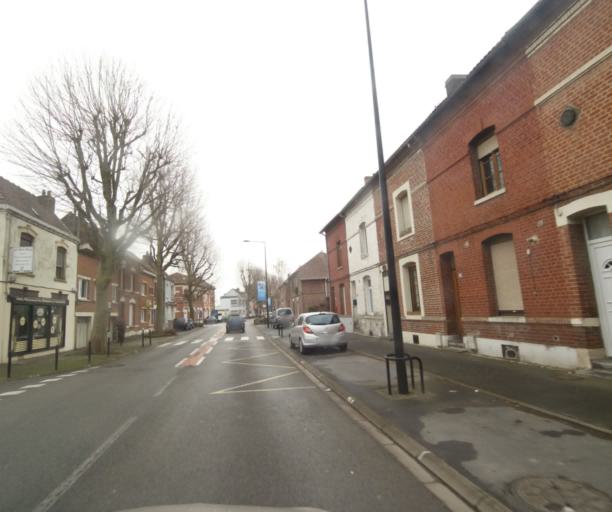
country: FR
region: Nord-Pas-de-Calais
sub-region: Departement du Nord
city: Valenciennes
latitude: 50.3455
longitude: 3.5255
